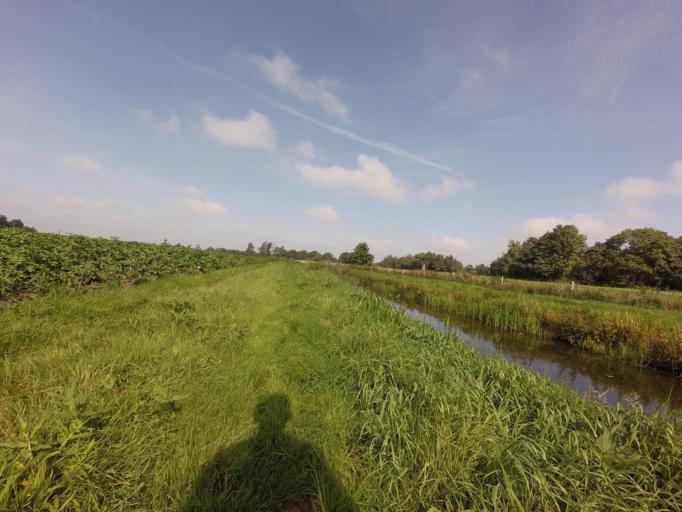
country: NL
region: Drenthe
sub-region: Gemeente Tynaarlo
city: Vries
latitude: 53.1204
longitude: 6.5442
